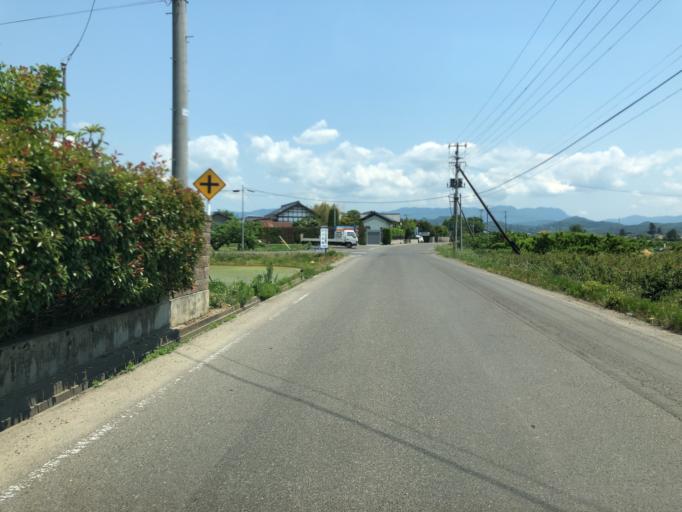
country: JP
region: Fukushima
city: Hobaramachi
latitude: 37.8323
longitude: 140.5477
